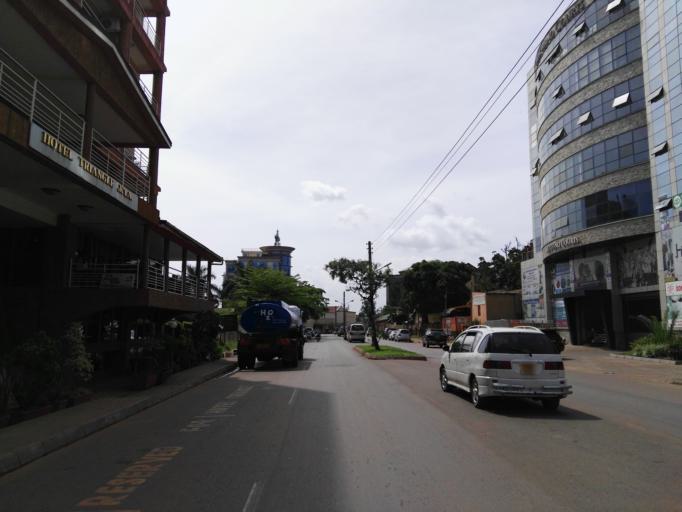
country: UG
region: Central Region
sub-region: Kampala District
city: Kampala
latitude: 0.3173
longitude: 32.5766
